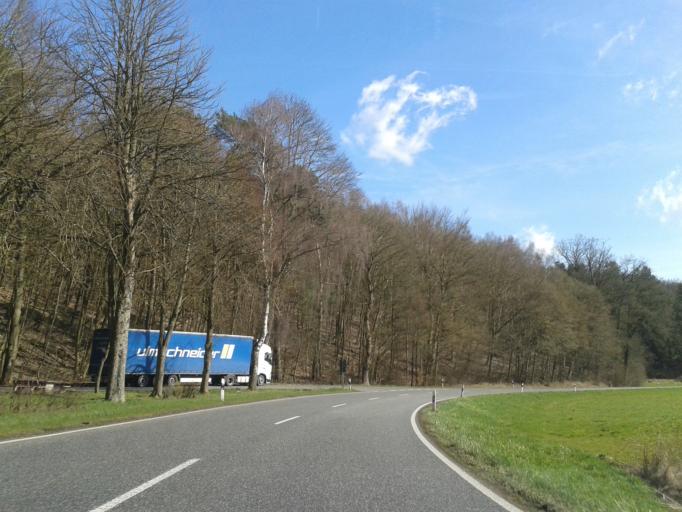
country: DE
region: Hesse
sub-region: Regierungsbezirk Giessen
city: Munchhausen
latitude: 50.9905
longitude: 8.6984
